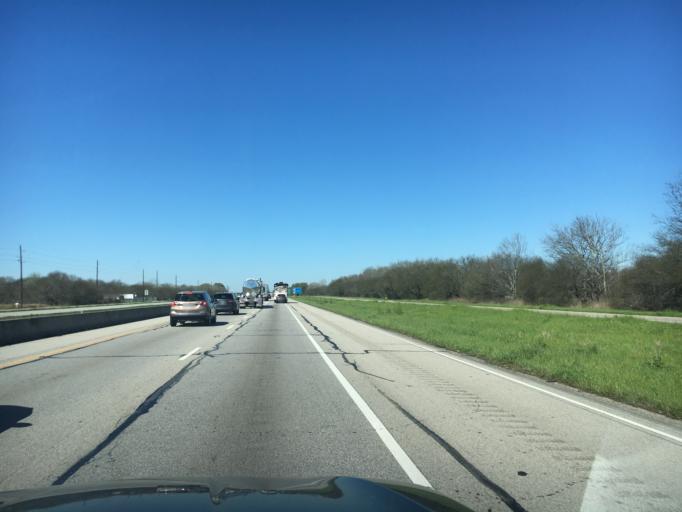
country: US
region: Texas
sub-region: Austin County
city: Sealy
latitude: 29.7756
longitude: -96.0910
